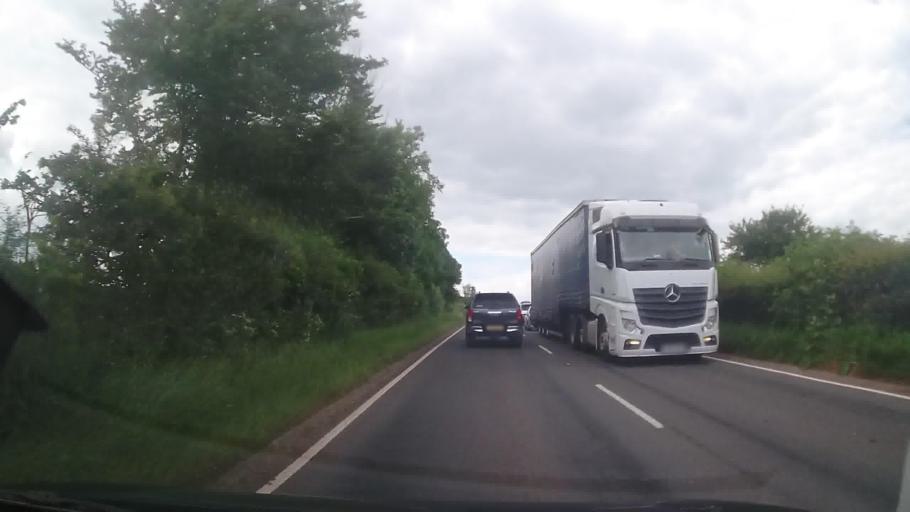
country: GB
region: England
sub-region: Herefordshire
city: Hereford
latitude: 52.0819
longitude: -2.7224
